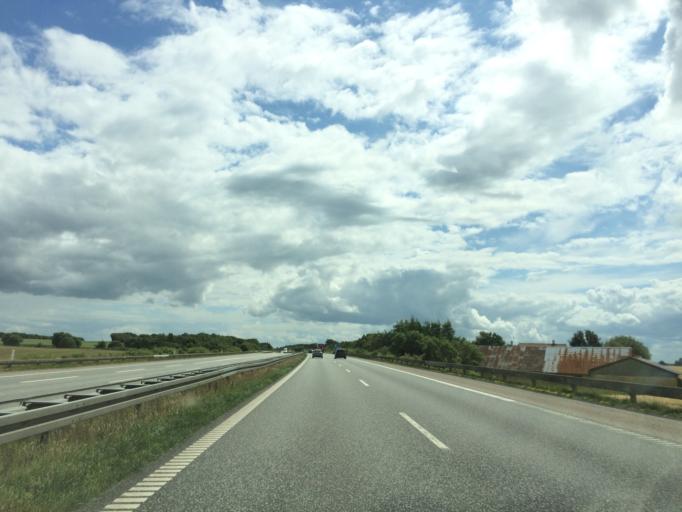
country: DK
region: North Denmark
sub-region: Mariagerfjord Kommune
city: Hobro
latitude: 56.7403
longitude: 9.7000
